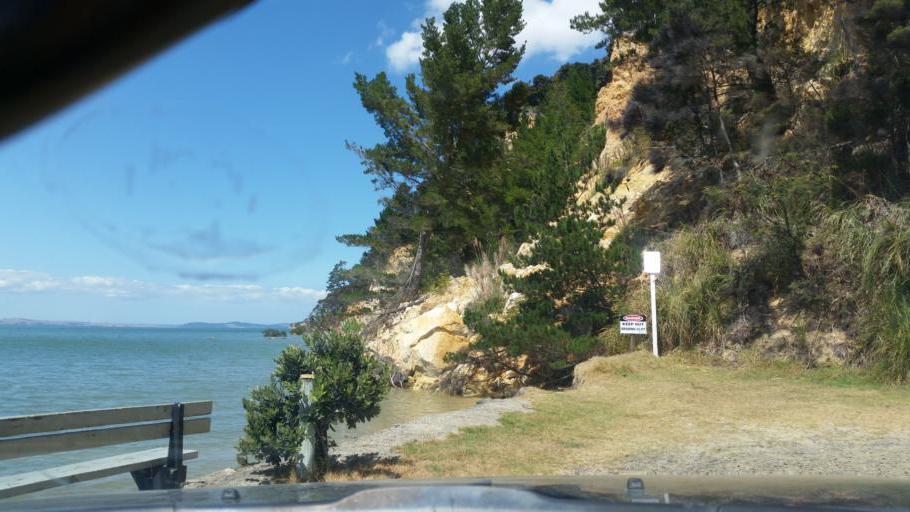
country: NZ
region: Northland
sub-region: Kaipara District
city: Dargaville
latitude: -36.2470
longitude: 174.1022
